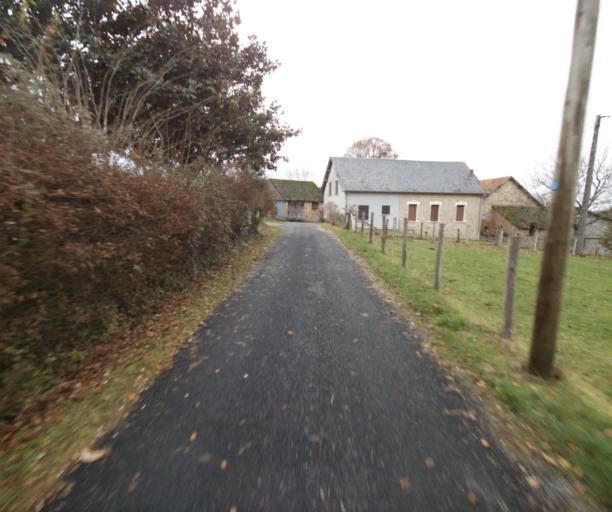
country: FR
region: Limousin
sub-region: Departement de la Correze
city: Chameyrat
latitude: 45.2383
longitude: 1.6626
